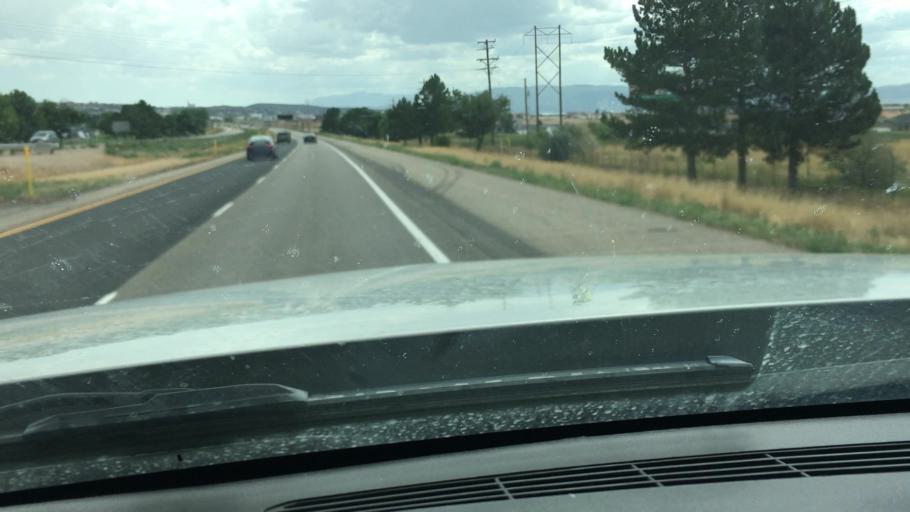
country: US
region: Utah
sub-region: Iron County
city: Cedar City
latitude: 37.7168
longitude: -113.0639
